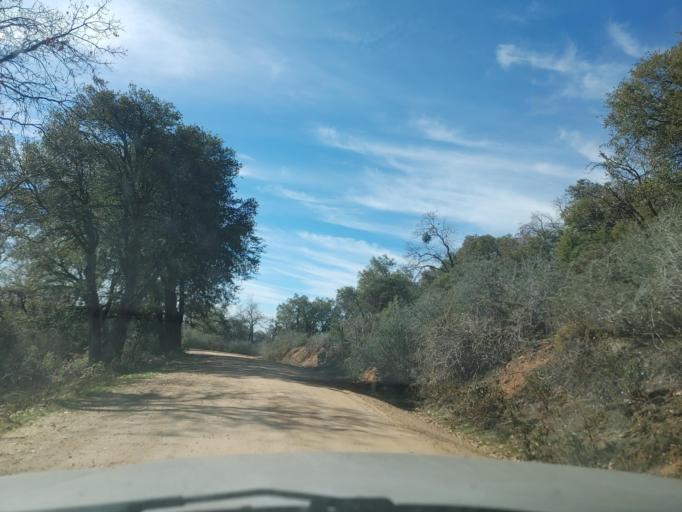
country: US
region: California
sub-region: Madera County
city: Ahwahnee
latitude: 37.4161
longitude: -119.6926
